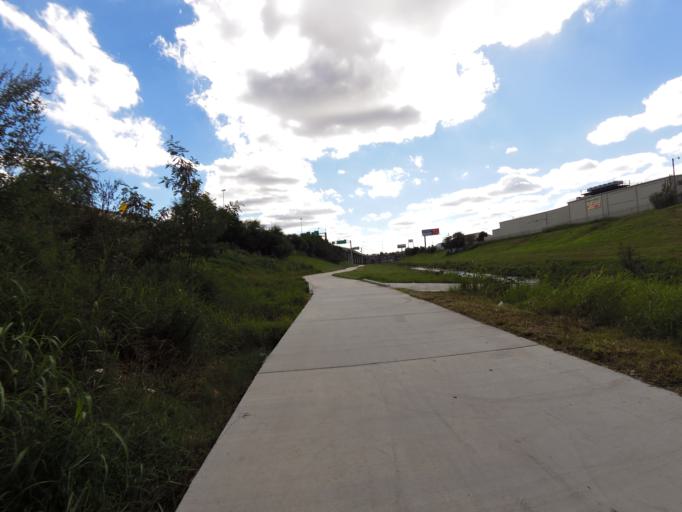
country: US
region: Texas
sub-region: Bexar County
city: San Antonio
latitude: 29.4113
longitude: -98.5088
